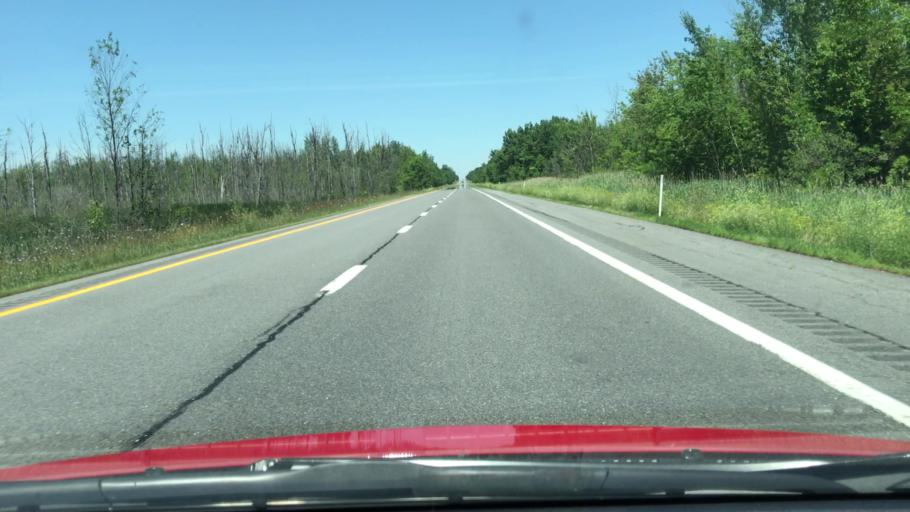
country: US
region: New York
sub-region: Clinton County
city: Champlain
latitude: 44.9421
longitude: -73.4473
